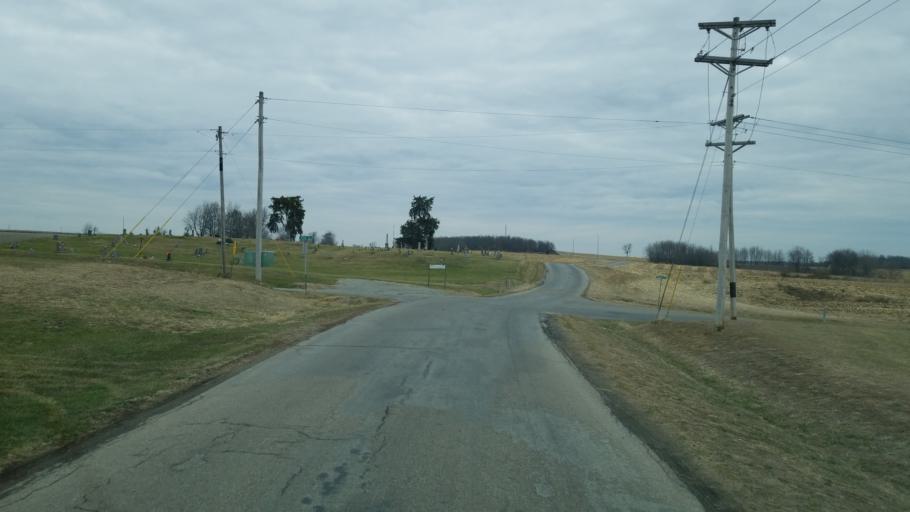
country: US
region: Ohio
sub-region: Highland County
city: Hillsboro
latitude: 39.2341
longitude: -83.4881
